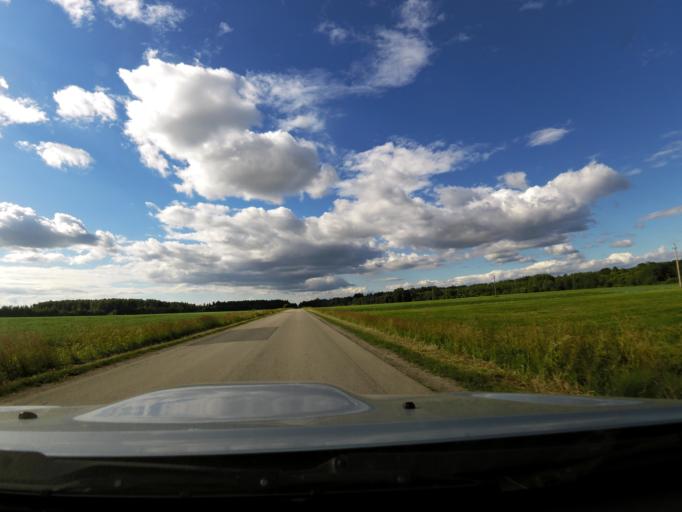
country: LT
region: Panevezys
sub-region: Birzai
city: Birzai
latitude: 56.3391
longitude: 24.8004
